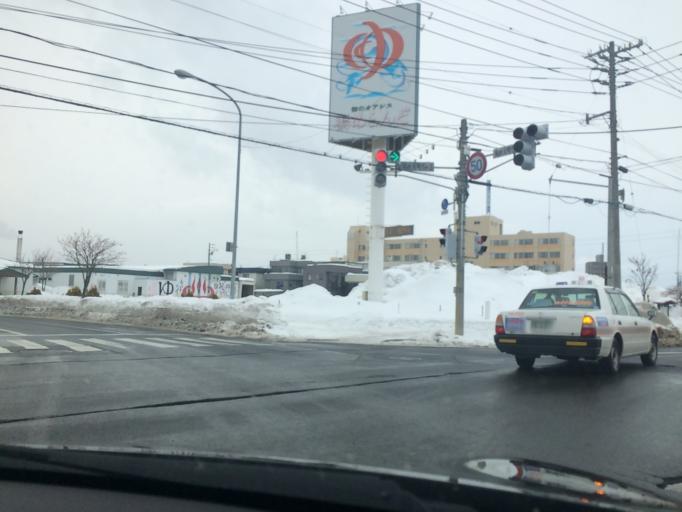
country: JP
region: Hokkaido
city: Sapporo
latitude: 43.0675
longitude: 141.4086
